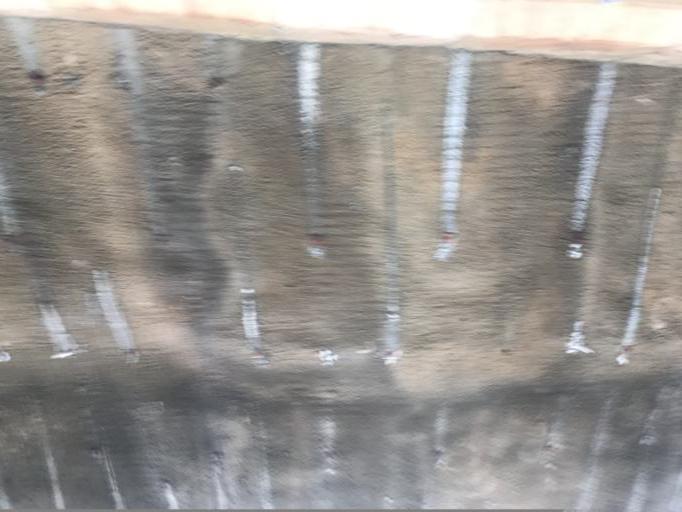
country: TR
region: Bartin
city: Amasra
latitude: 41.7184
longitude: 32.3954
